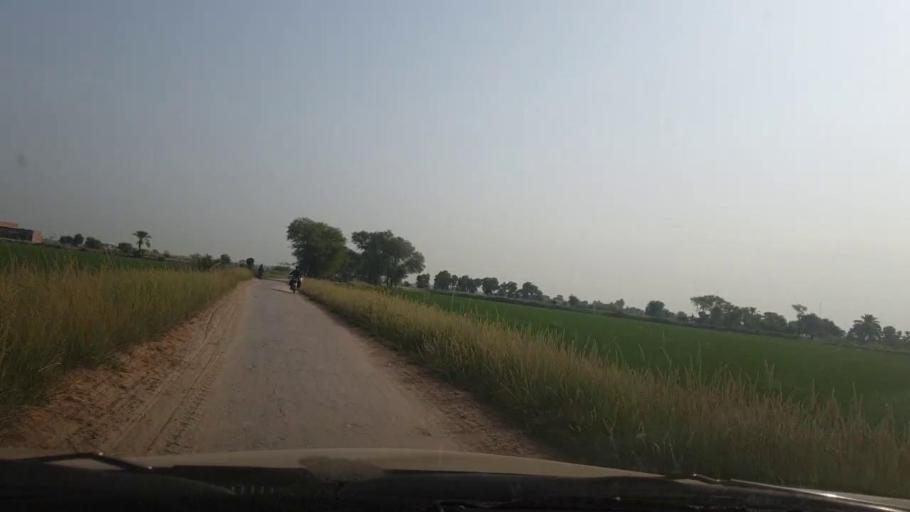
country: PK
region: Sindh
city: Larkana
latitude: 27.5878
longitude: 68.1880
